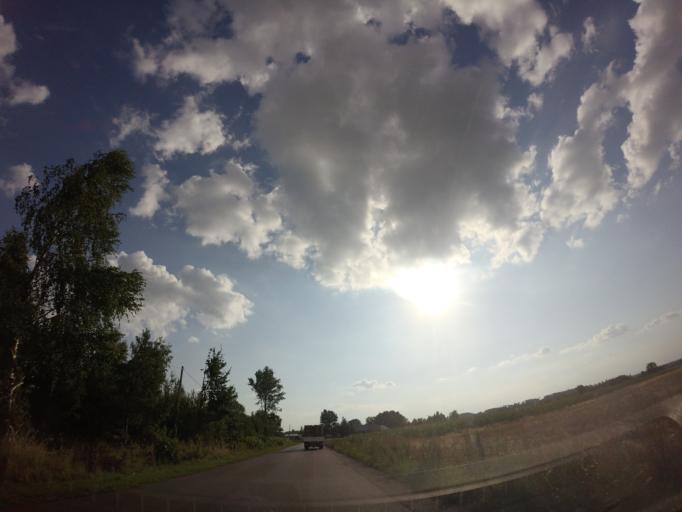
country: PL
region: Lublin Voivodeship
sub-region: Powiat lukowski
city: Adamow
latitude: 51.7549
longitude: 22.2673
